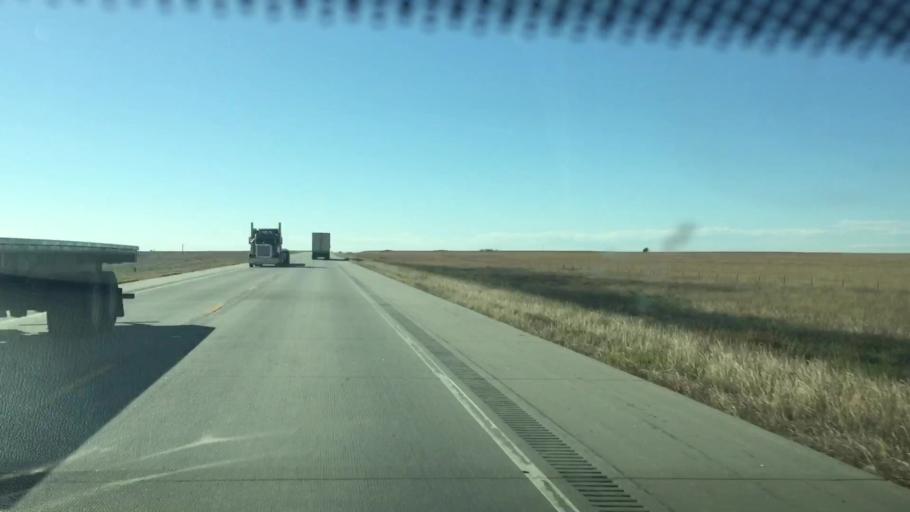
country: US
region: Colorado
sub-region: Kiowa County
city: Eads
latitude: 38.7653
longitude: -102.8397
